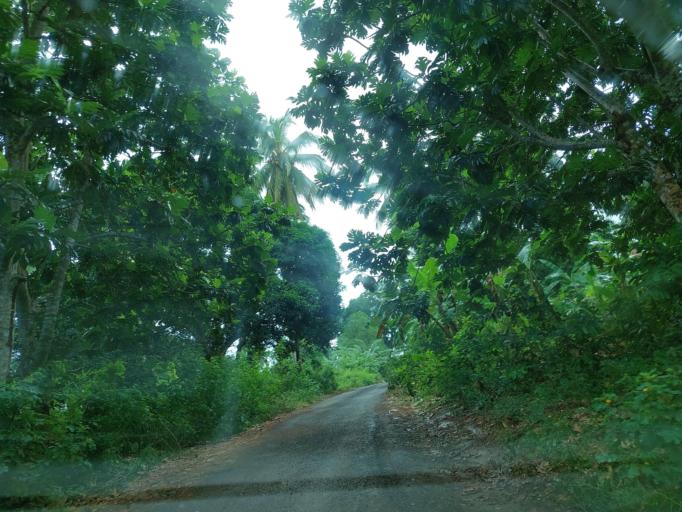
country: YT
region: Tsingoni
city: Tsingoni
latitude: -12.7560
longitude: 45.1245
